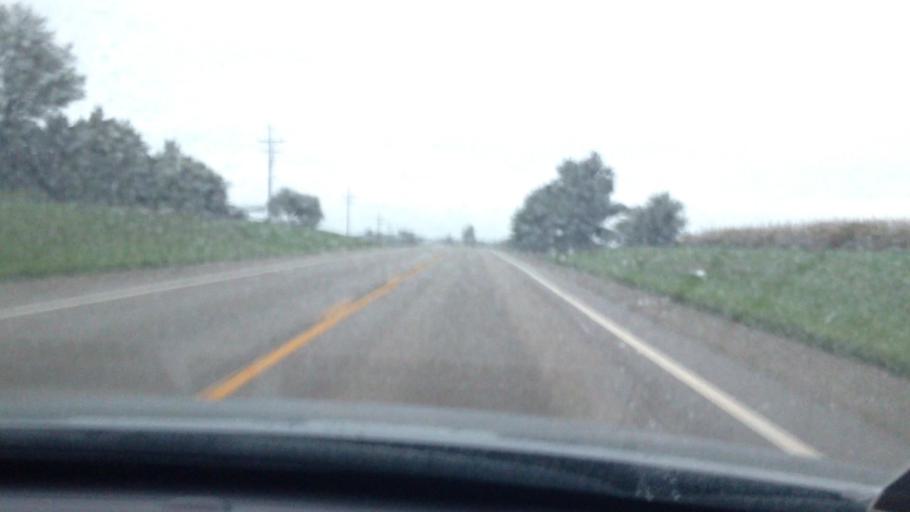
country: US
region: Kansas
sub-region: Brown County
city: Hiawatha
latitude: 39.8172
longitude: -95.5272
